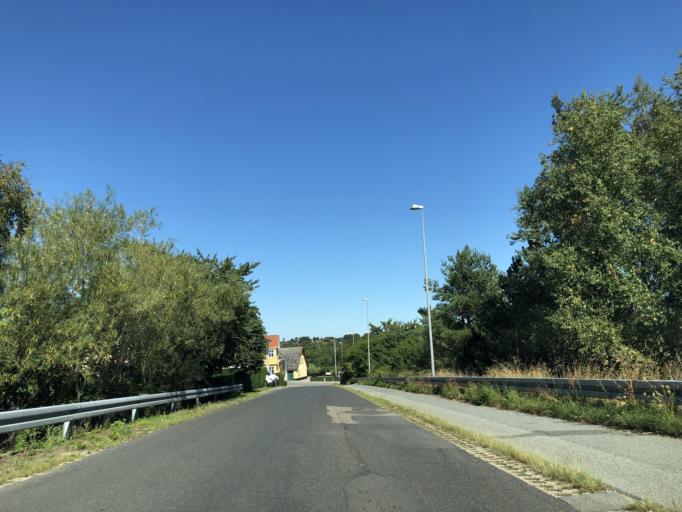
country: DK
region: North Denmark
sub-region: Mariagerfjord Kommune
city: Hobro
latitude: 56.6475
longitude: 9.7800
